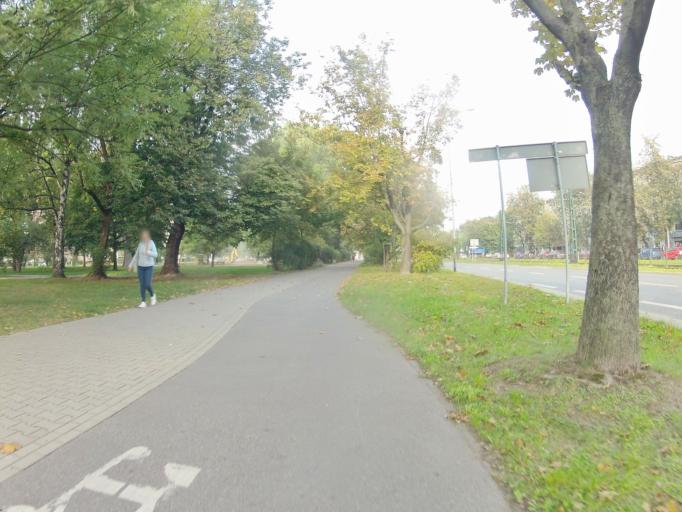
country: PL
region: Lesser Poland Voivodeship
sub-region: Powiat wielicki
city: Kokotow
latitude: 50.0806
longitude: 20.0293
